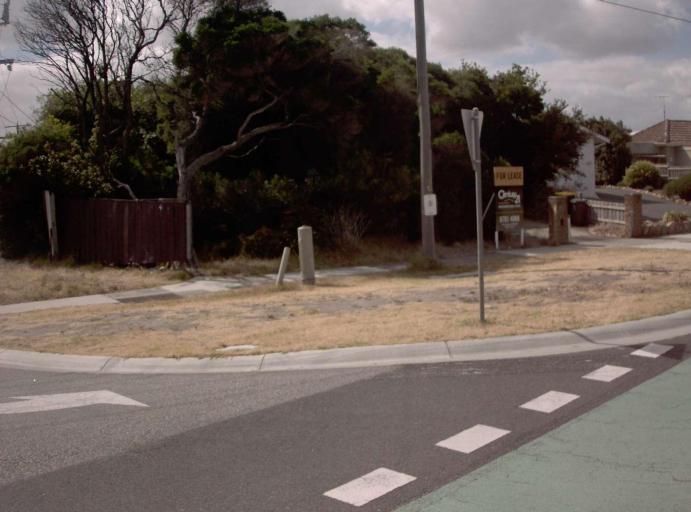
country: AU
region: Victoria
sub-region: Frankston
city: Frankston East
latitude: -38.1305
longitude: 145.1251
